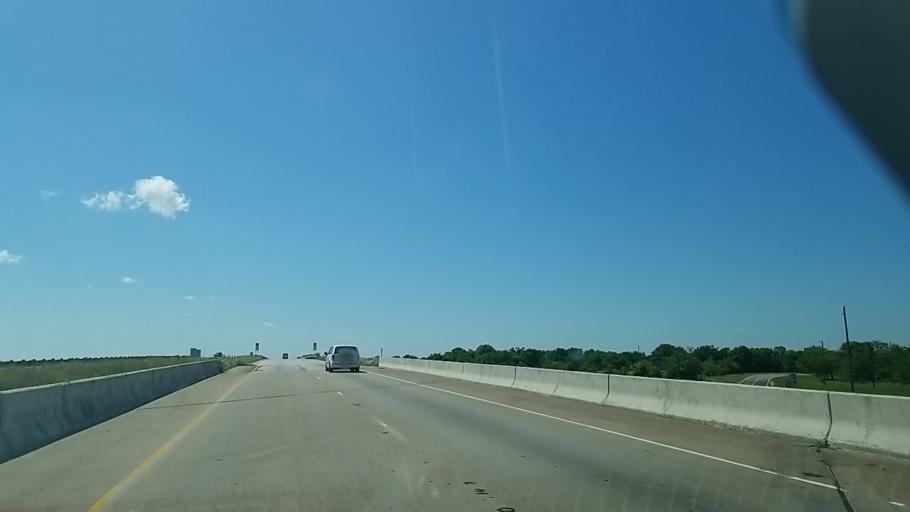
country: US
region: Texas
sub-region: Freestone County
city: Wortham
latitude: 31.8641
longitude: -96.3198
